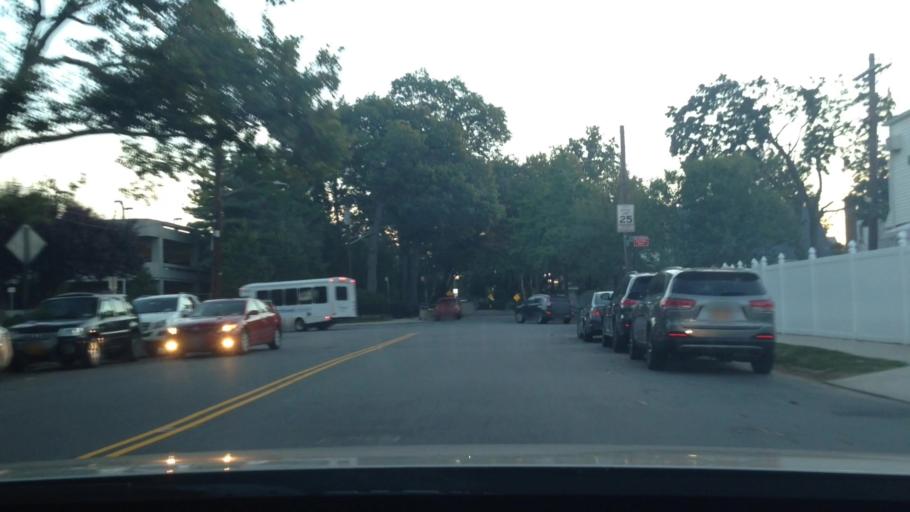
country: US
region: New York
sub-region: Nassau County
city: North New Hyde Park
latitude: 40.7535
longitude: -73.7066
